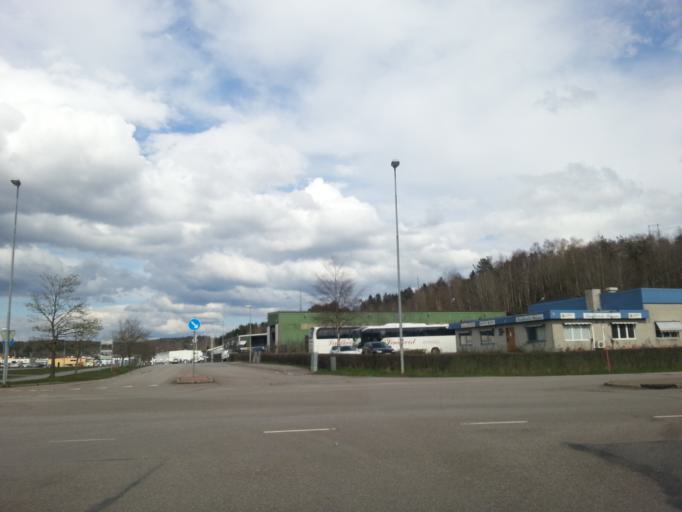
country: SE
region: Vaestra Goetaland
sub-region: Kungalvs Kommun
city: Kungalv
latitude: 57.8719
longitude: 11.9422
